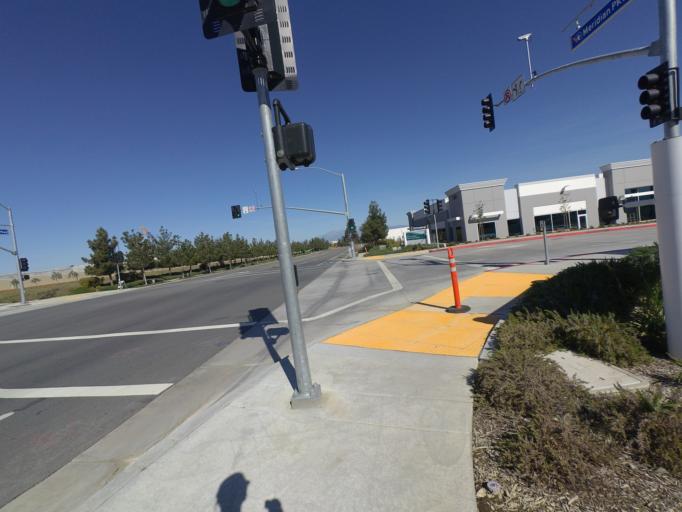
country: US
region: California
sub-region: Riverside County
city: March Air Force Base
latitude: 33.9119
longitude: -117.2895
